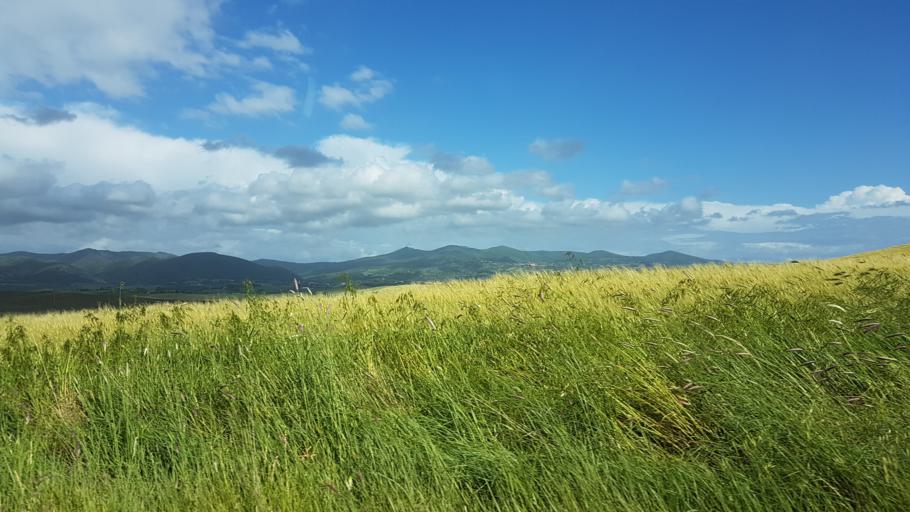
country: IT
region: Tuscany
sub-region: Province of Pisa
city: Orciano Pisano
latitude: 43.4471
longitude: 10.5103
